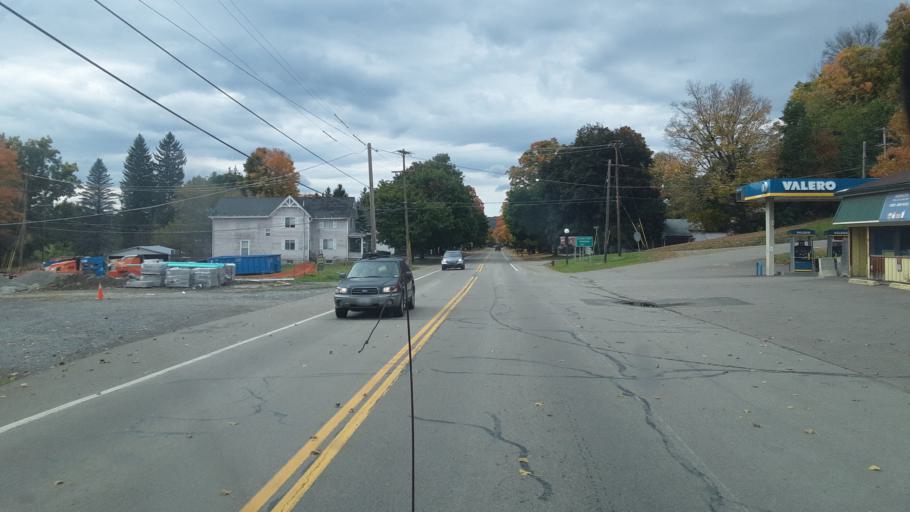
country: US
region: New York
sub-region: Allegany County
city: Belmont
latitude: 42.3040
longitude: -78.0082
